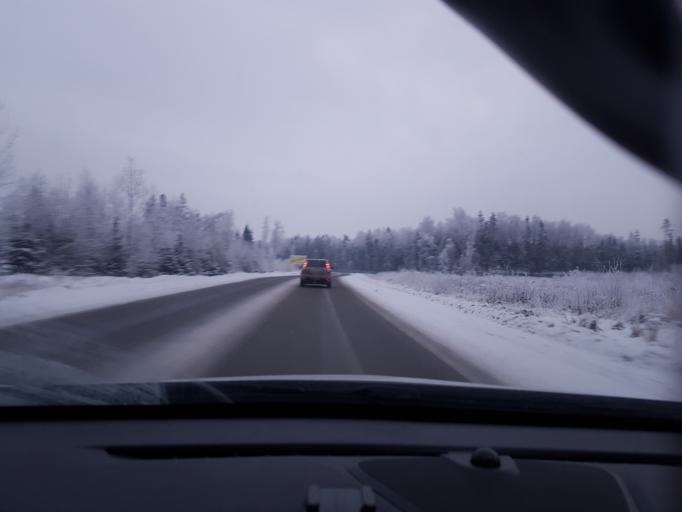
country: RU
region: Moskovskaya
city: Rozhdestveno
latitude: 55.8347
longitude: 37.0182
